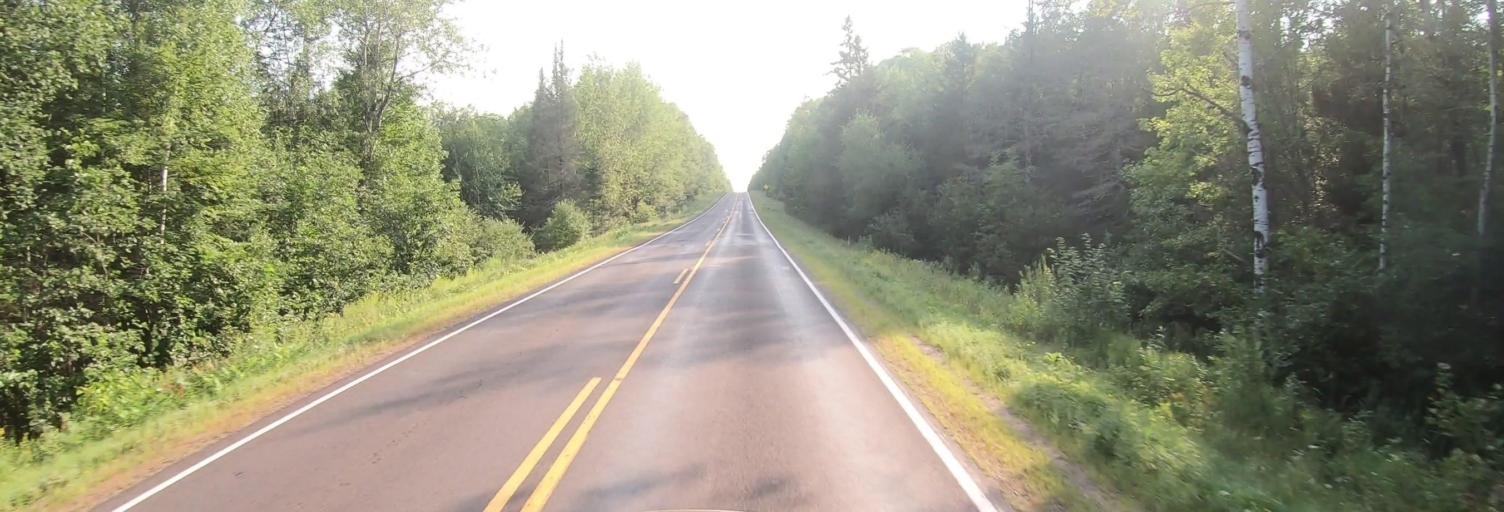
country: US
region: Wisconsin
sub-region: Ashland County
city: Ashland
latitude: 46.1899
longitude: -90.8829
